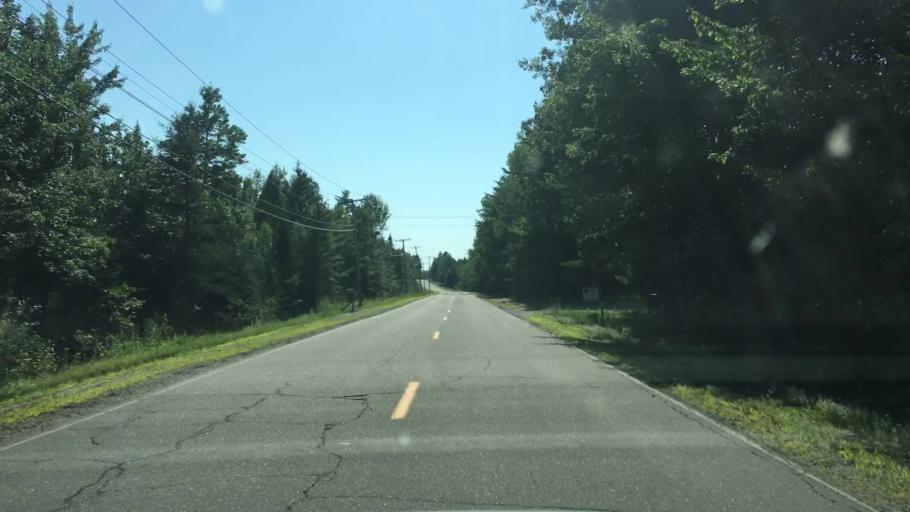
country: US
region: Maine
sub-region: Penobscot County
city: Enfield
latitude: 45.2449
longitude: -68.6094
